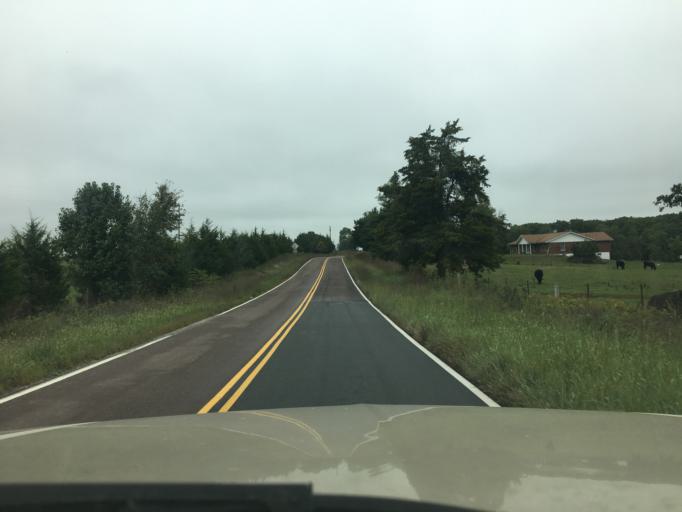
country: US
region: Missouri
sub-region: Crawford County
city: Cuba
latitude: 38.1784
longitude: -91.4894
